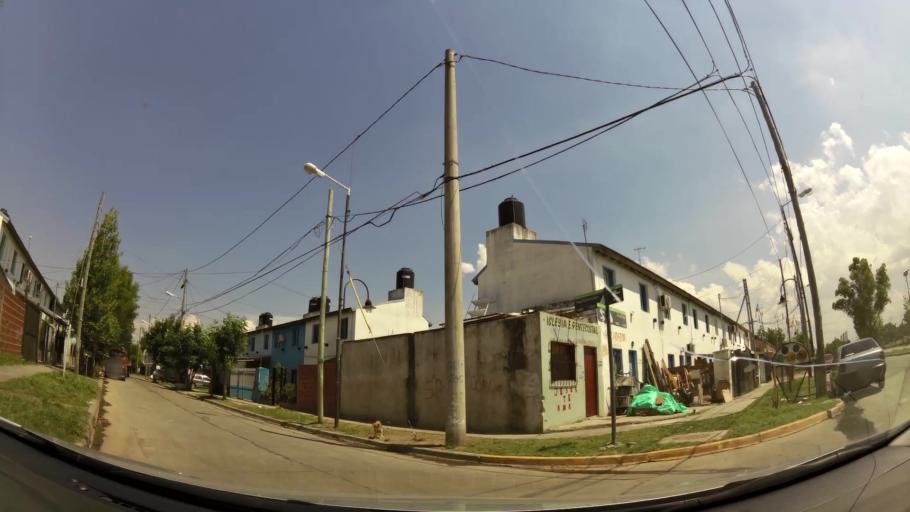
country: AR
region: Buenos Aires
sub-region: Partido de Tigre
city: Tigre
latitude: -34.4569
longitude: -58.5806
